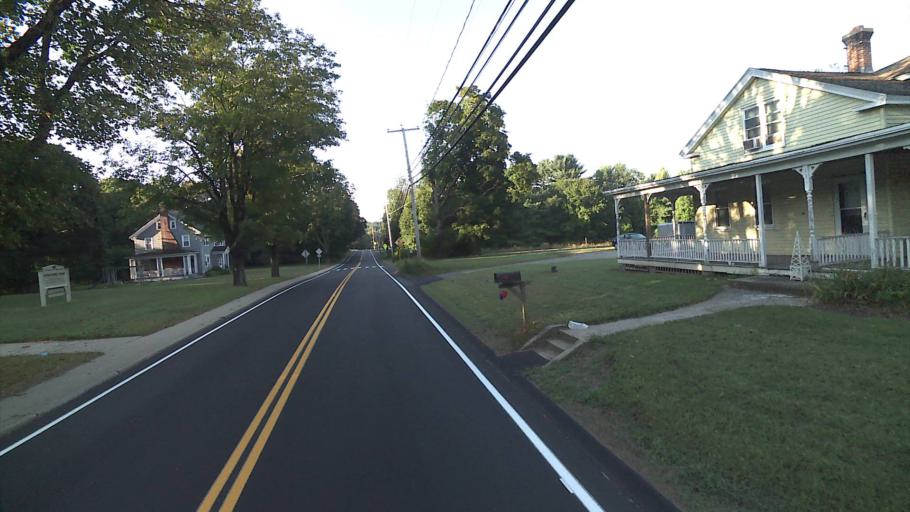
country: US
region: Connecticut
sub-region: Tolland County
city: Storrs
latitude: 41.8541
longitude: -72.3011
